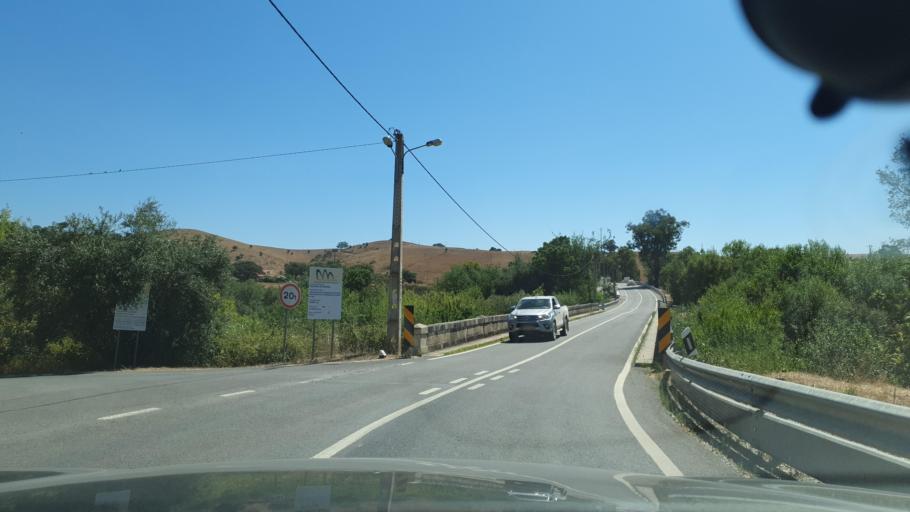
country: PT
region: Beja
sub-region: Odemira
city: Odemira
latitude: 37.4935
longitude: -8.4837
